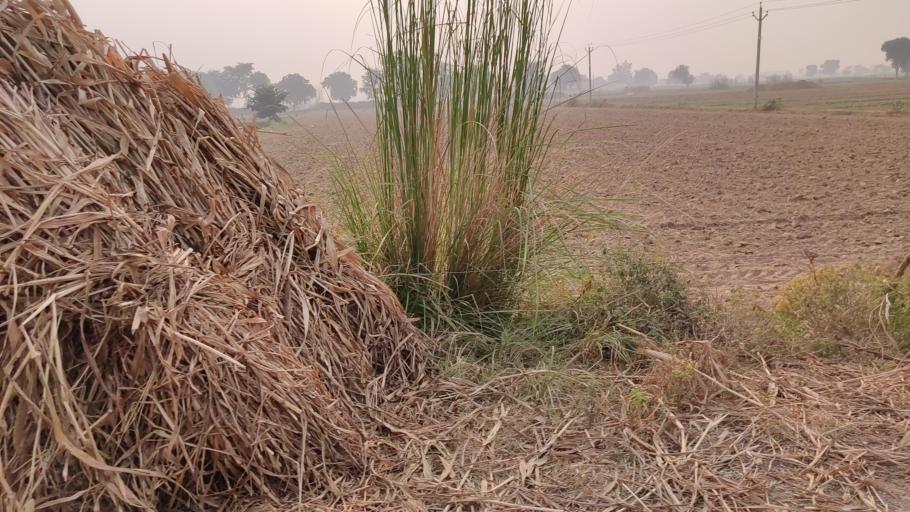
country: IN
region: Uttar Pradesh
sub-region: Mathura
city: Vrindavan
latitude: 27.5524
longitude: 77.7135
